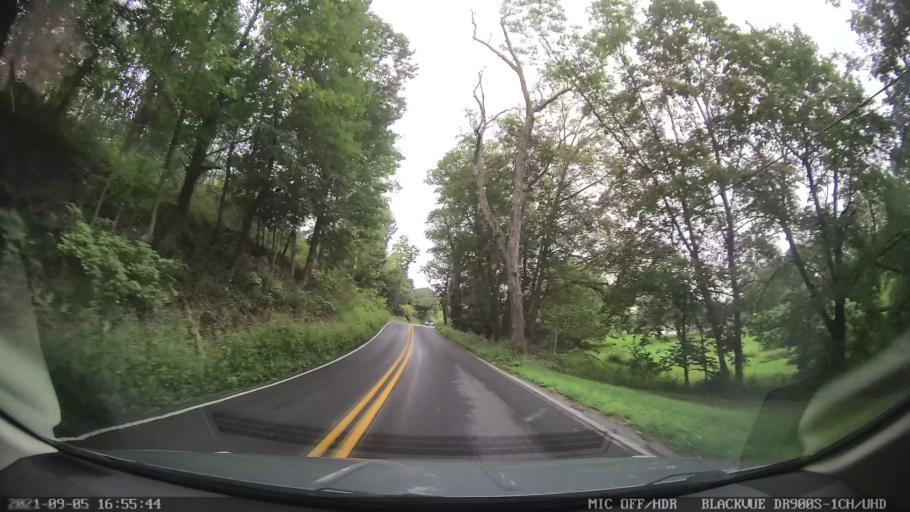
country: US
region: Pennsylvania
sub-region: Lehigh County
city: Wescosville
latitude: 40.6109
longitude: -75.5917
